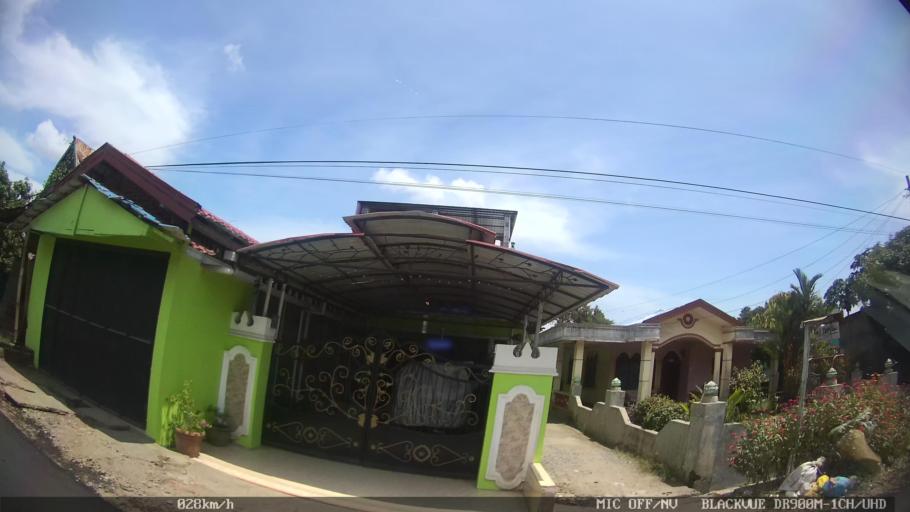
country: ID
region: North Sumatra
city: Binjai
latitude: 3.5913
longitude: 98.5005
